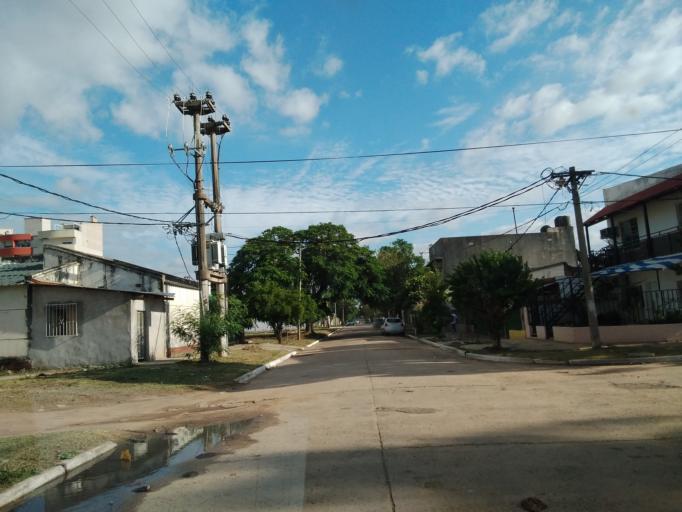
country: AR
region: Corrientes
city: Corrientes
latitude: -27.4575
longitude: -58.8188
